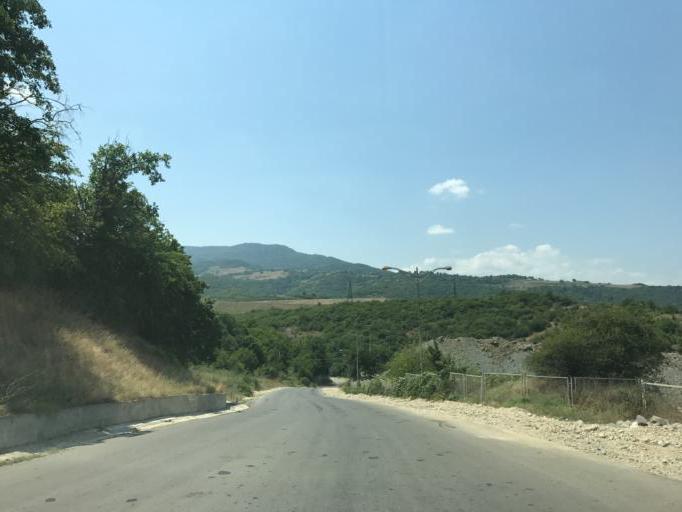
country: AZ
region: Tartar Rayon
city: Martakert
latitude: 40.1432
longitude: 46.5963
